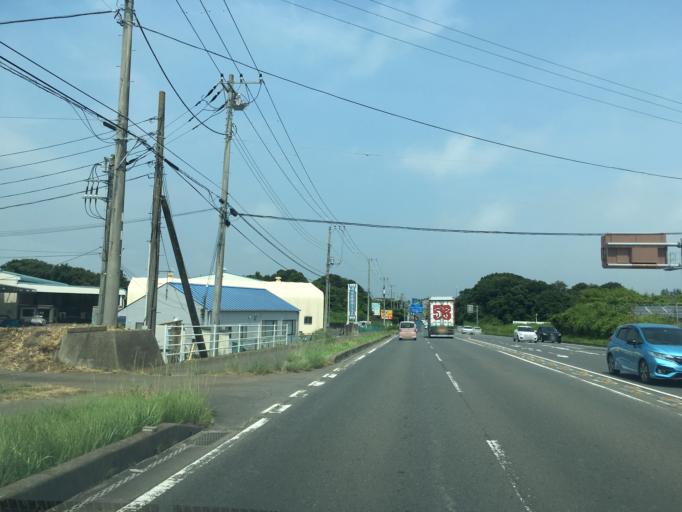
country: JP
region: Ibaraki
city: Katsuta
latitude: 36.3738
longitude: 140.5786
